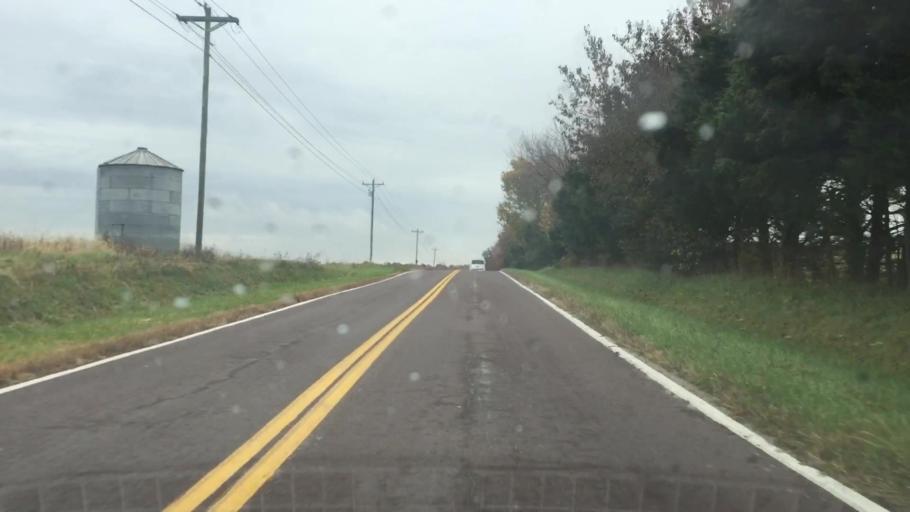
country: US
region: Missouri
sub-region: Callaway County
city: Fulton
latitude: 38.7879
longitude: -91.7840
